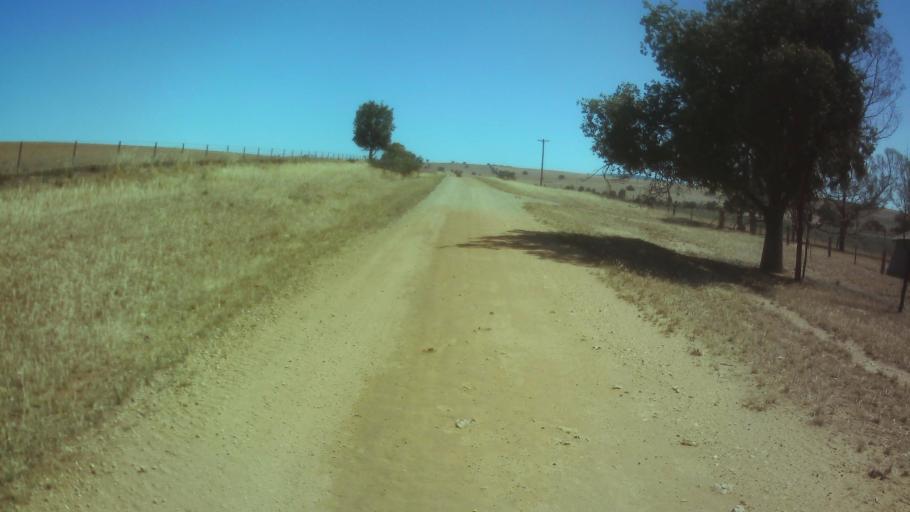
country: AU
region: New South Wales
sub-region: Weddin
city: Grenfell
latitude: -33.9852
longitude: 148.3583
